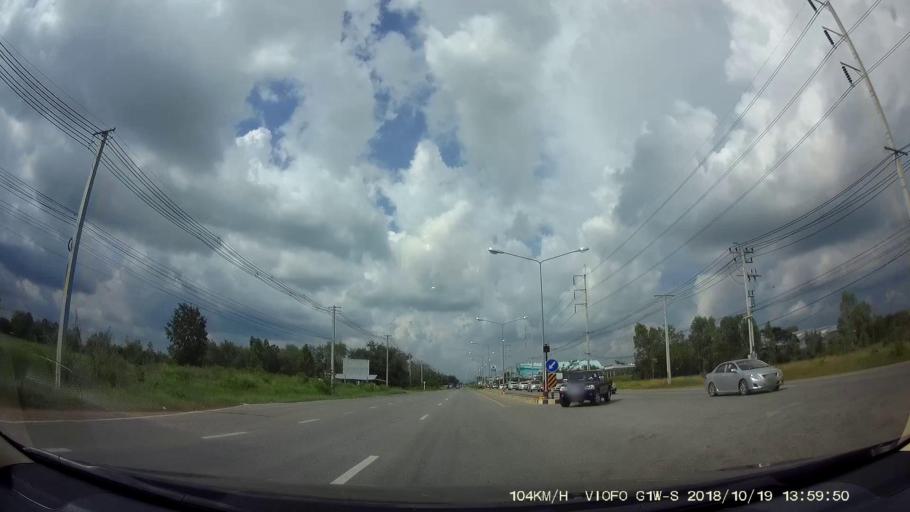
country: TH
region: Chaiyaphum
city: Chaiyaphum
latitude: 15.8157
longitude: 102.0602
